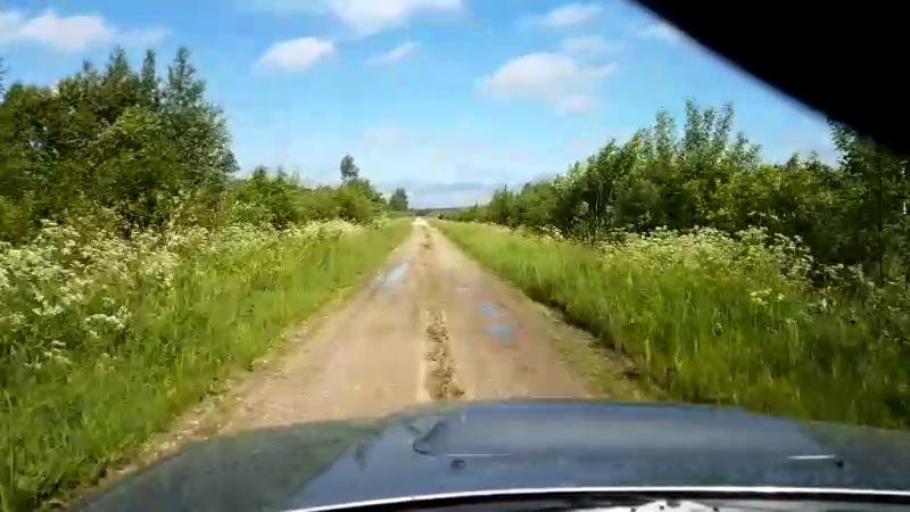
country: EE
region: Paernumaa
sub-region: Sindi linn
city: Sindi
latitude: 58.4875
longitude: 24.6602
